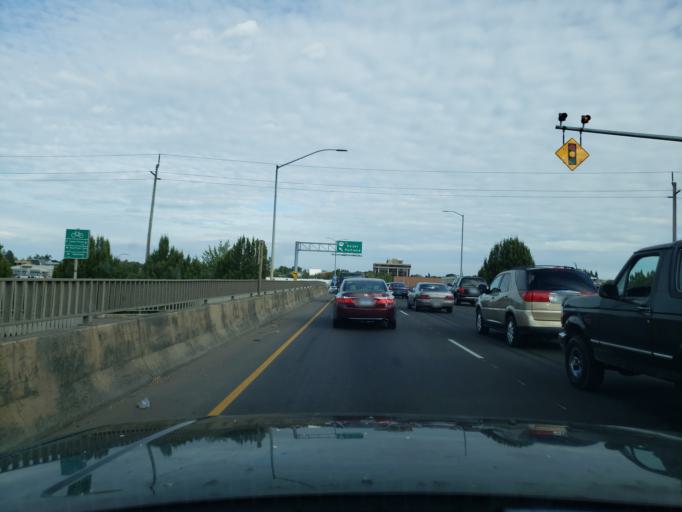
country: US
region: Oregon
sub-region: Marion County
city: Salem
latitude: 44.9445
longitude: -123.0415
